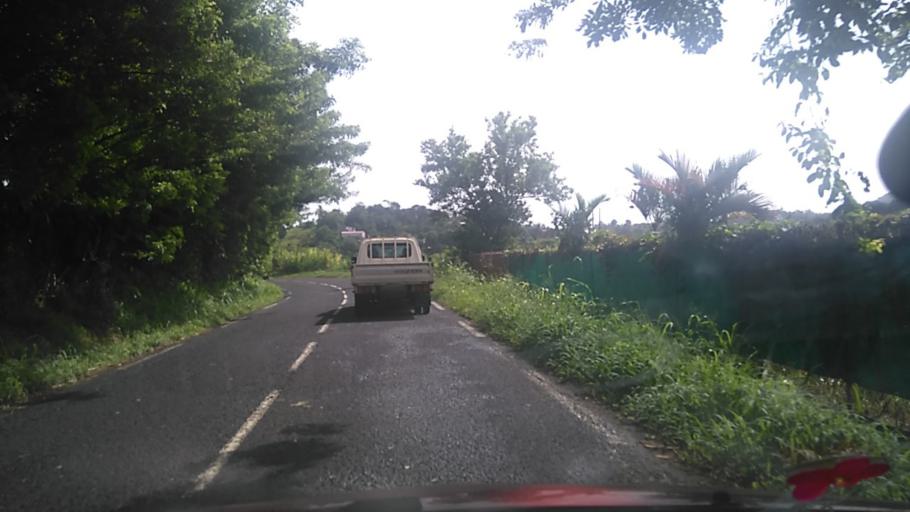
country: MQ
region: Martinique
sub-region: Martinique
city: Saint-Esprit
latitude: 14.5837
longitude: -60.9241
